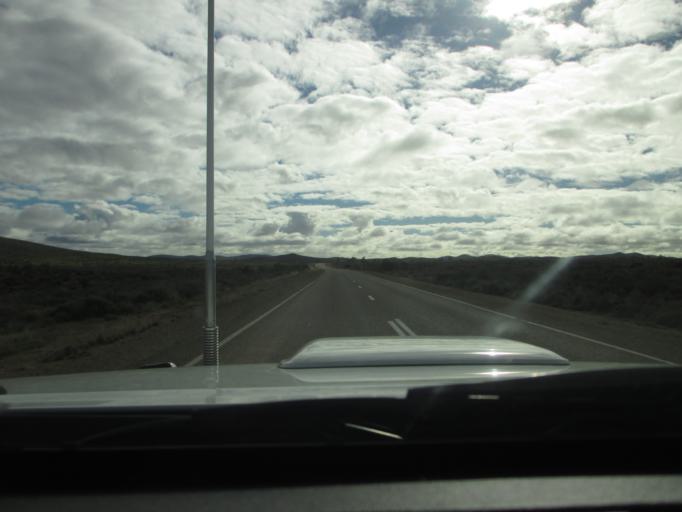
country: AU
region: South Australia
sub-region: Flinders Ranges
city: Quorn
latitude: -32.2923
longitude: 138.4911
